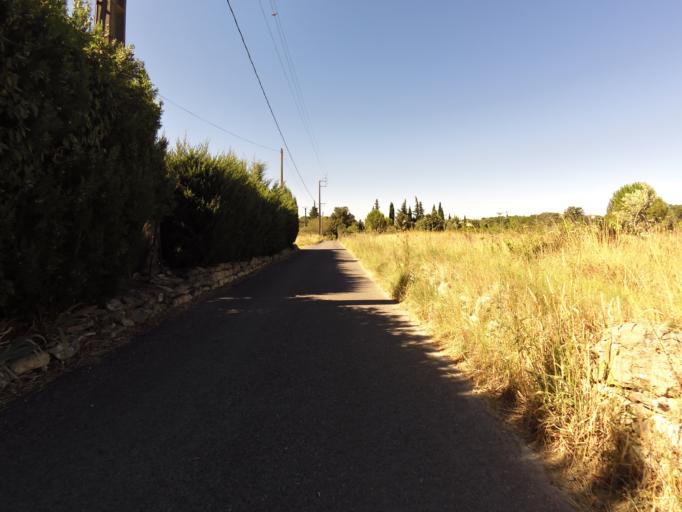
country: FR
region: Languedoc-Roussillon
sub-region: Departement du Gard
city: Congenies
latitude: 43.7524
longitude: 4.1661
